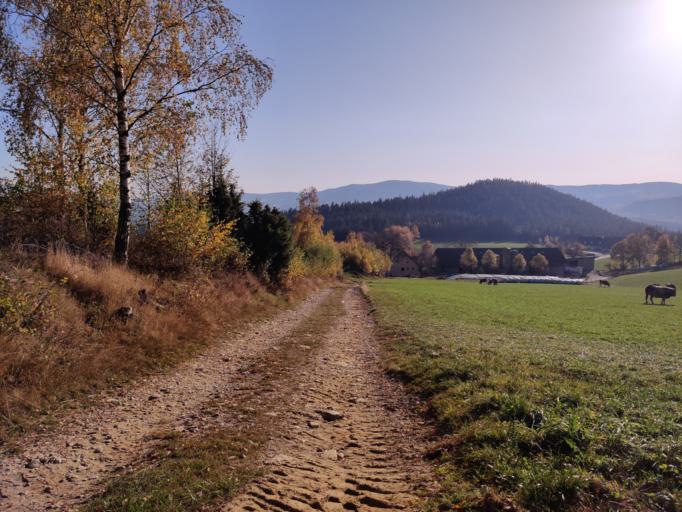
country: AT
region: Styria
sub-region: Politischer Bezirk Hartberg-Fuerstenfeld
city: Sankt Jakob im Walde
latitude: 47.4679
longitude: 15.8102
